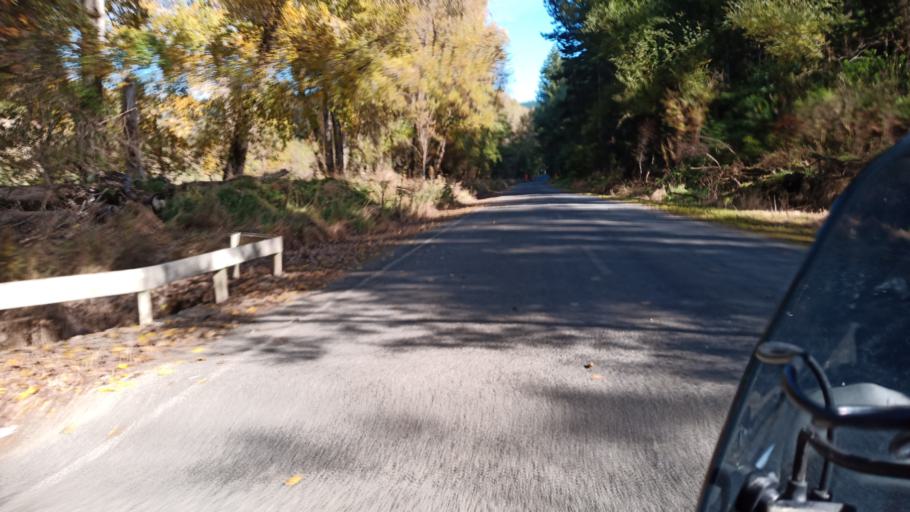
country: NZ
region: Hawke's Bay
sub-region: Wairoa District
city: Wairoa
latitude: -38.9205
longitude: 177.2500
